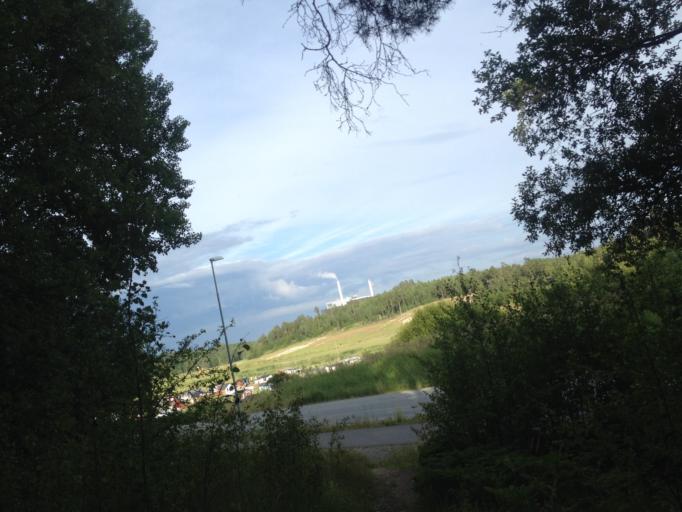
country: SE
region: Stockholm
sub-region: Sigtuna Kommun
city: Marsta
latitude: 59.6132
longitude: 17.8418
